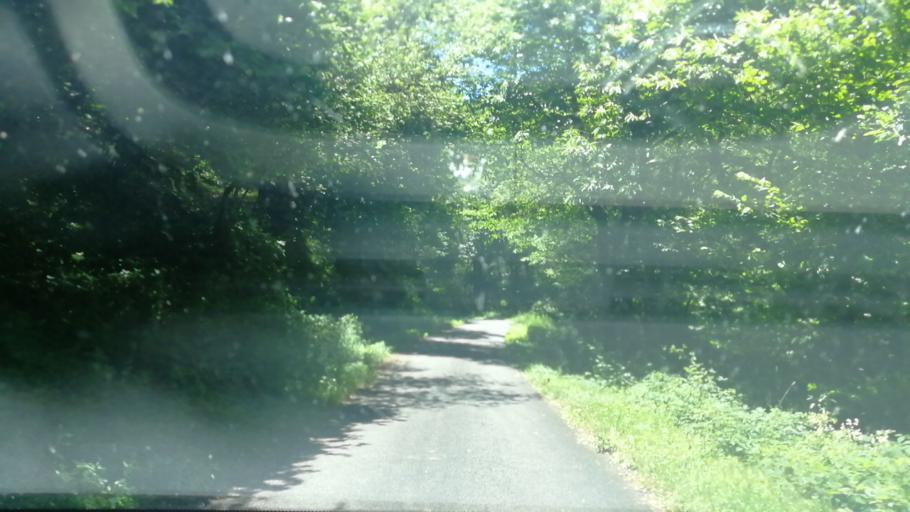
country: FR
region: Midi-Pyrenees
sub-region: Departement de l'Aveyron
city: Firmi
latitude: 44.5839
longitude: 2.3805
